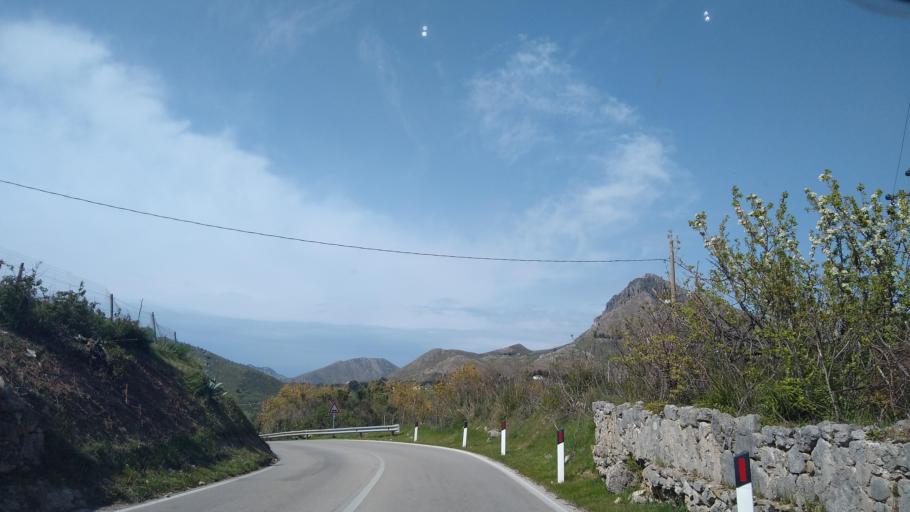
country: IT
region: Sicily
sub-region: Palermo
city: Pioppo
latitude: 38.0411
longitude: 13.1996
